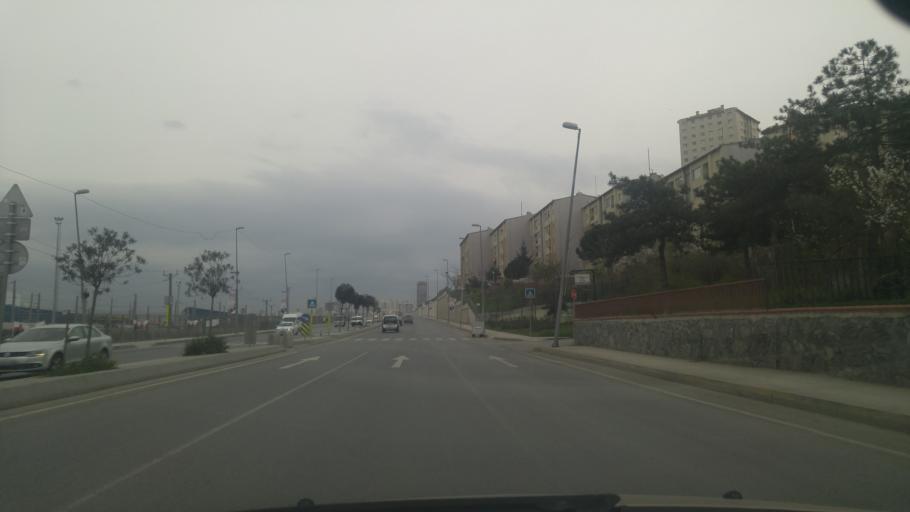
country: TR
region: Istanbul
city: Mahmutbey
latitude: 41.0215
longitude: 28.7676
